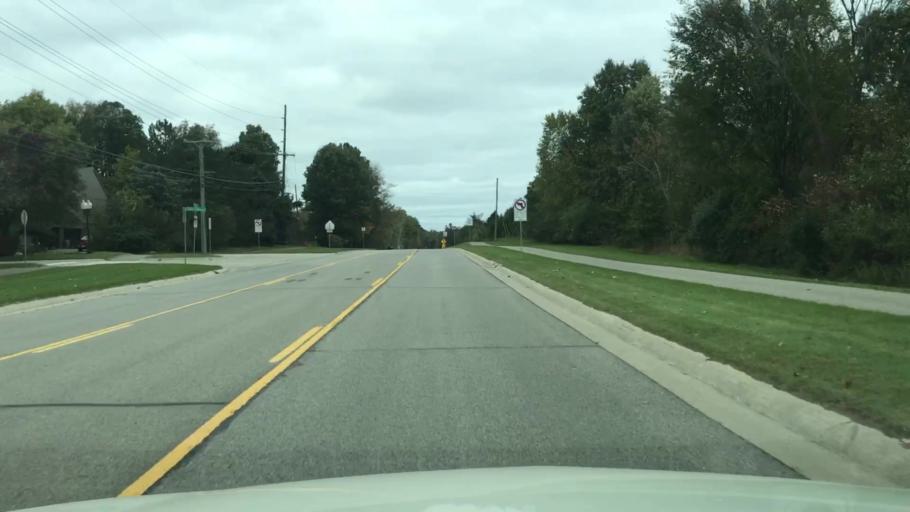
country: US
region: Michigan
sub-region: Oakland County
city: Rochester
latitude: 42.7028
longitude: -83.1240
